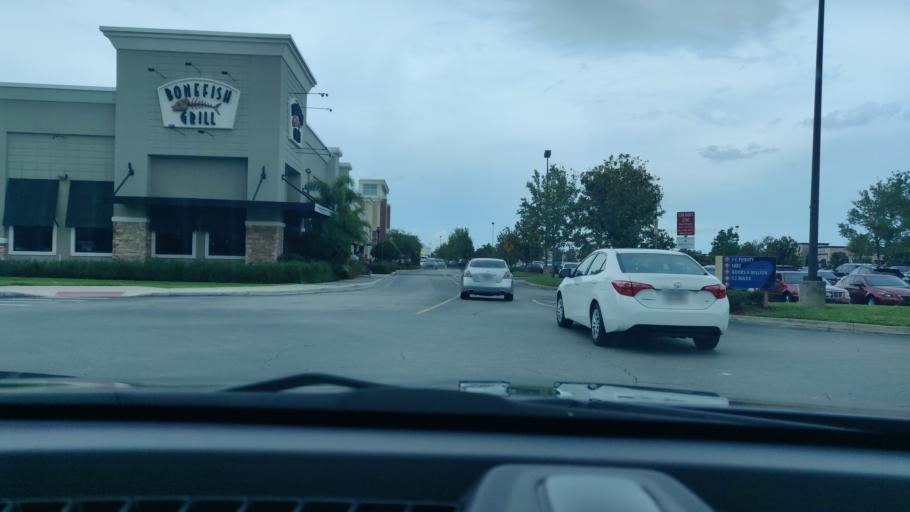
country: US
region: Florida
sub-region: Orange County
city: Hunters Creek
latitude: 28.3434
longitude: -81.4300
